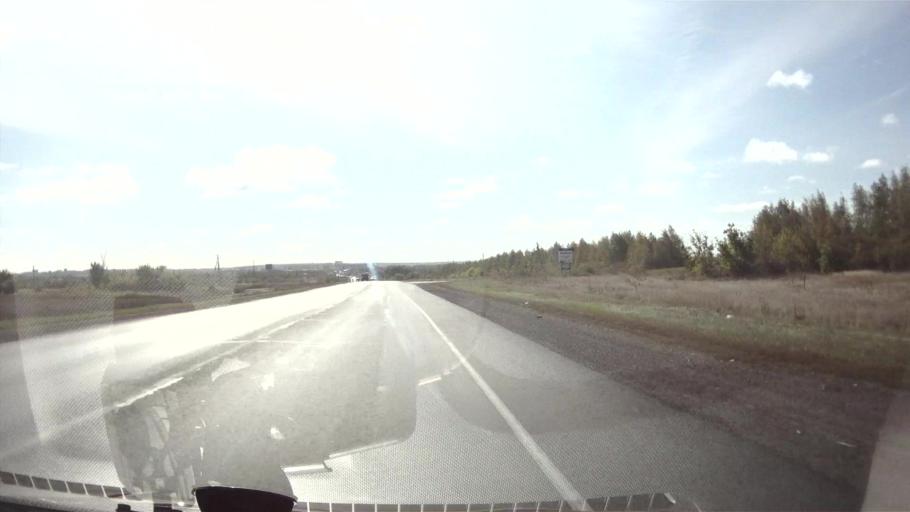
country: RU
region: Ulyanovsk
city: Isheyevka
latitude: 54.3127
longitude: 48.2350
